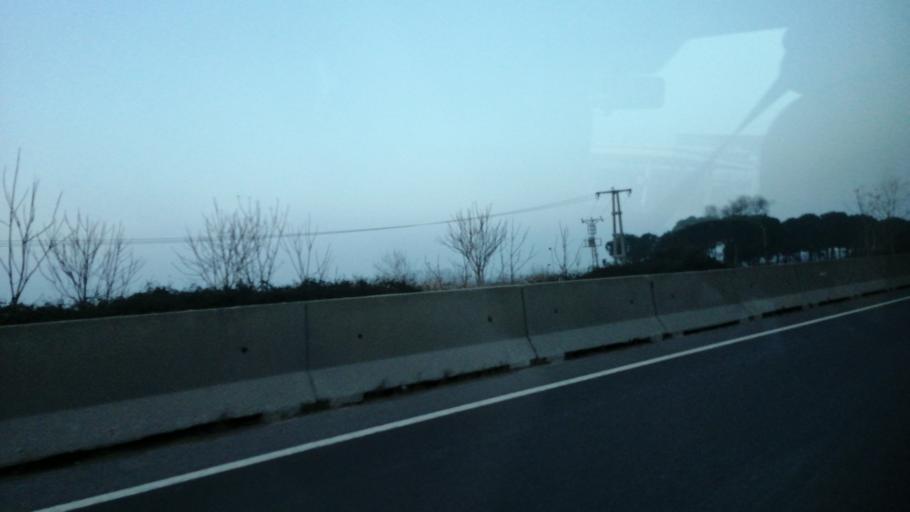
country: TR
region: Yalova
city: Taskopru
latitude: 40.6861
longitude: 29.4126
